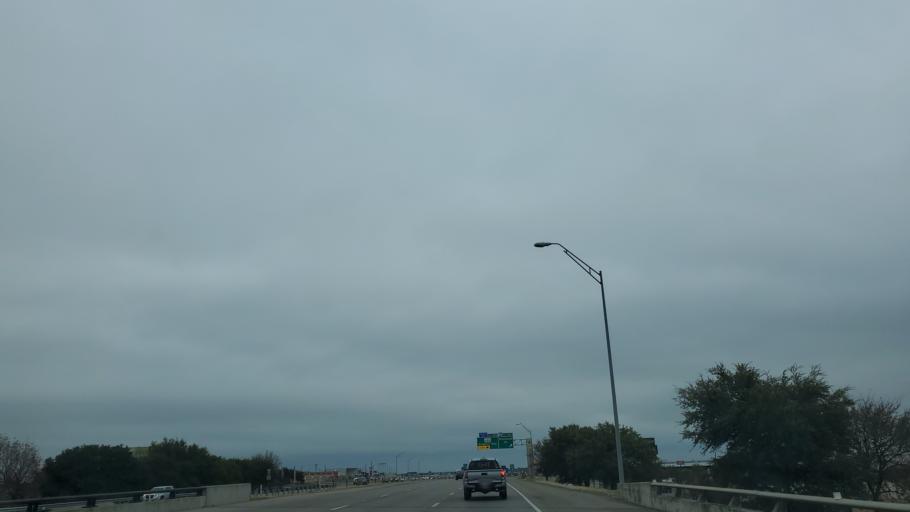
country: US
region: Texas
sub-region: Bell County
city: Harker Heights
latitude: 31.0803
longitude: -97.6987
